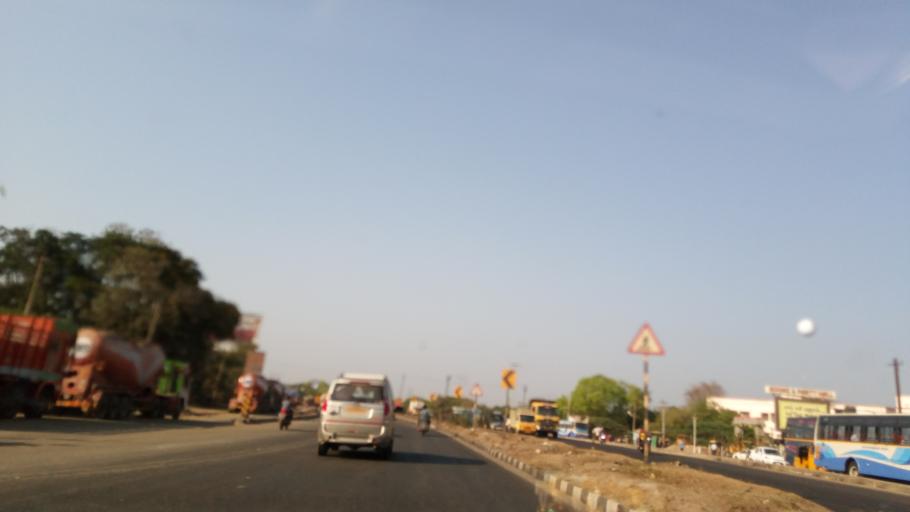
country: IN
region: Tamil Nadu
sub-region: Kancheepuram
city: Poonamalle
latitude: 13.0502
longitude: 80.0888
